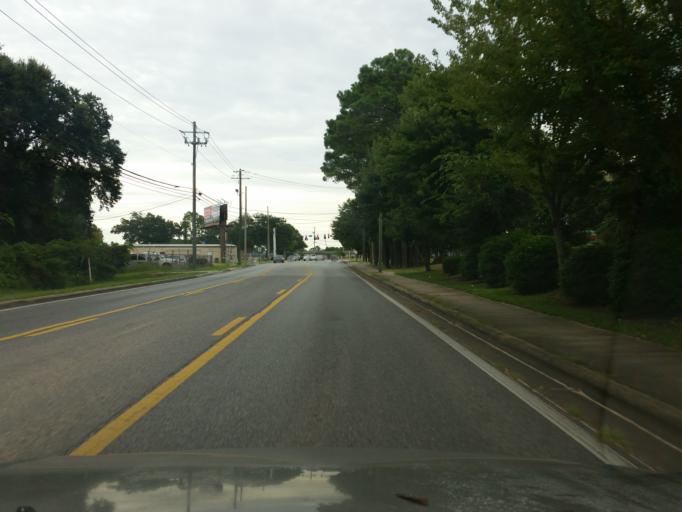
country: US
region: Florida
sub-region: Escambia County
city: Brent
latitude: 30.4808
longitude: -87.2607
